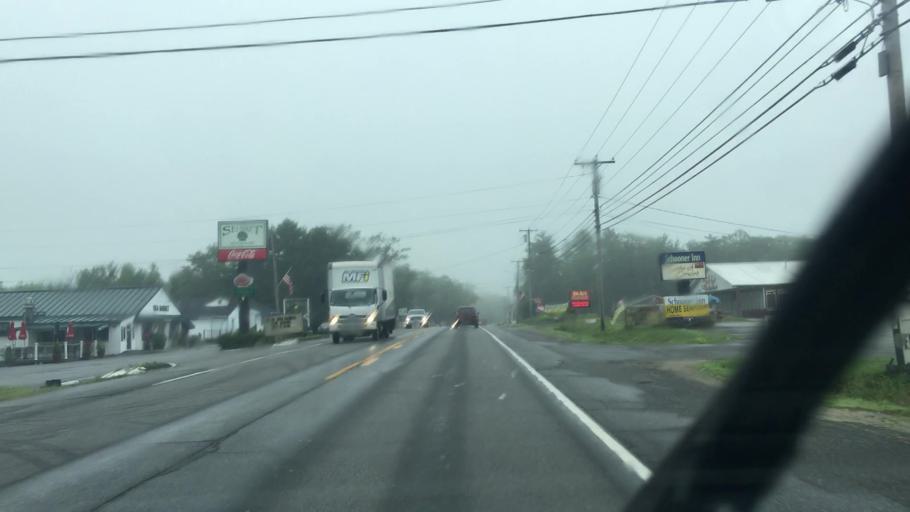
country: US
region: Maine
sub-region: Lincoln County
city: Wiscasset
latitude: 43.9926
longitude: -69.6882
